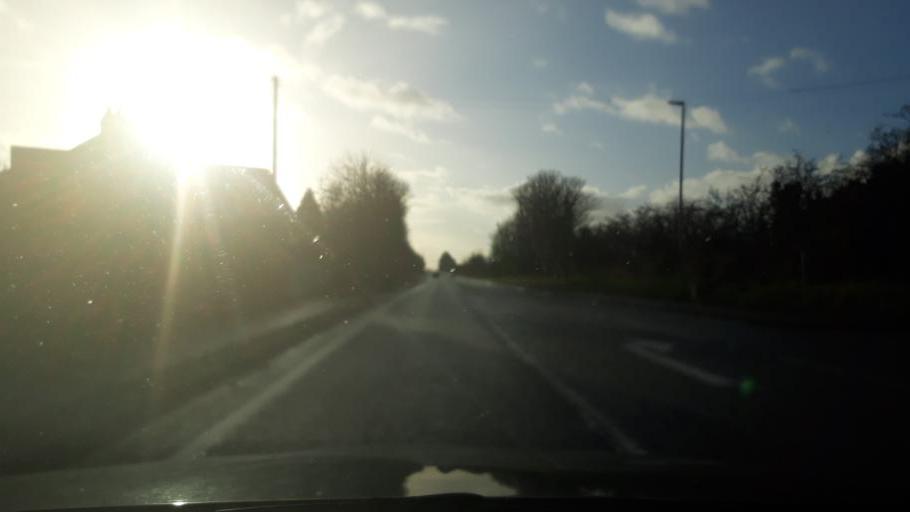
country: GB
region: Northern Ireland
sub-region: Coleraine District
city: Coleraine
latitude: 55.1147
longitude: -6.6864
